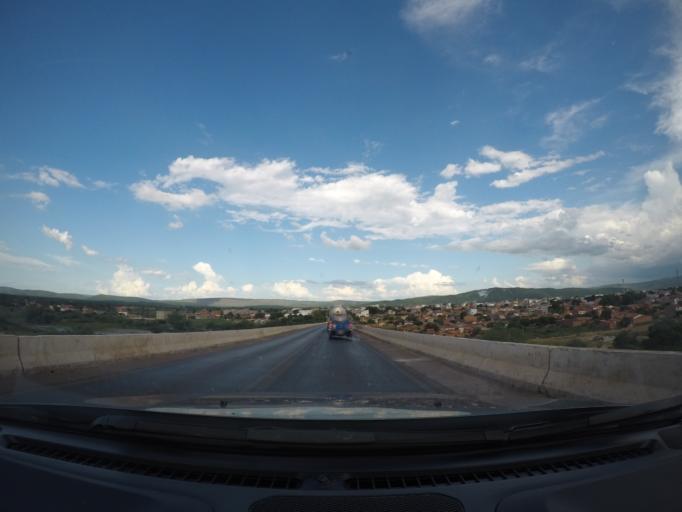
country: BR
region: Bahia
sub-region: Ibotirama
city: Ibotirama
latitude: -12.1798
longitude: -43.2248
